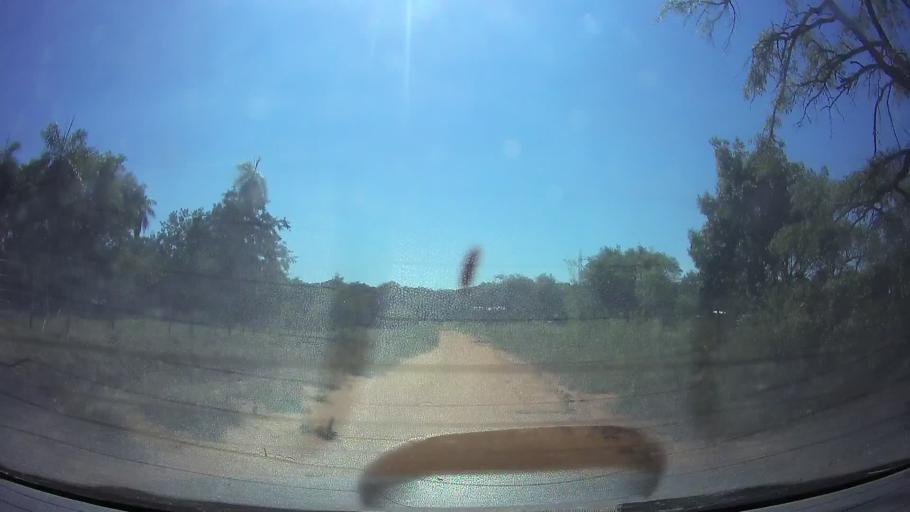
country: PY
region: Central
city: Limpio
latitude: -25.2379
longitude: -57.4408
